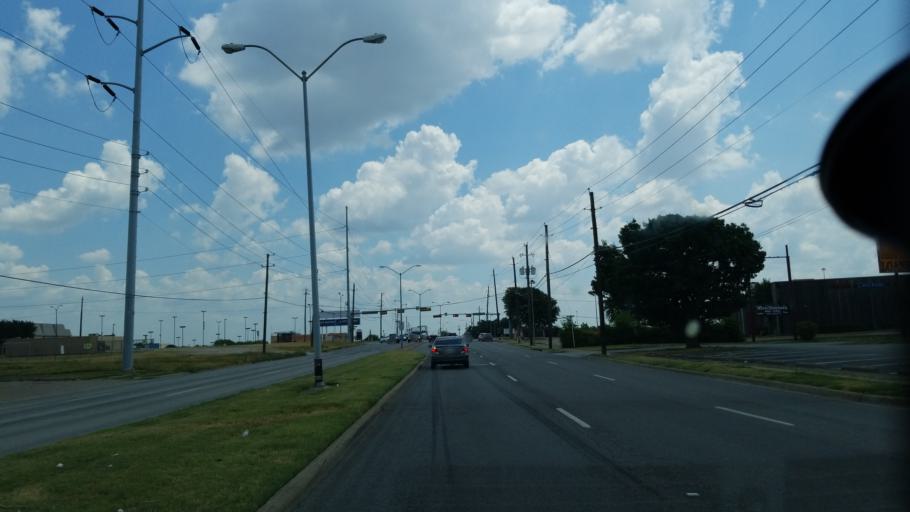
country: US
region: Texas
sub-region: Dallas County
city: Duncanville
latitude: 32.6620
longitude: -96.8832
